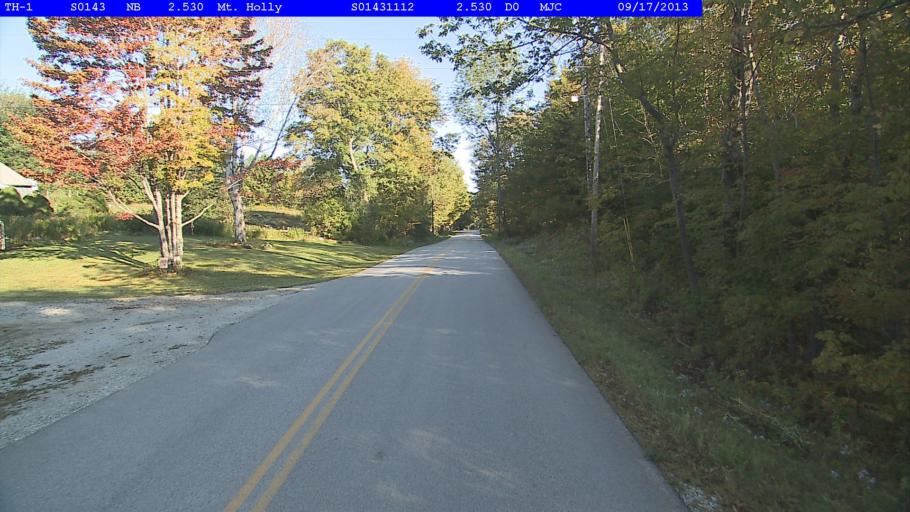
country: US
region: Vermont
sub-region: Rutland County
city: Rutland
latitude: 43.4341
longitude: -72.8258
